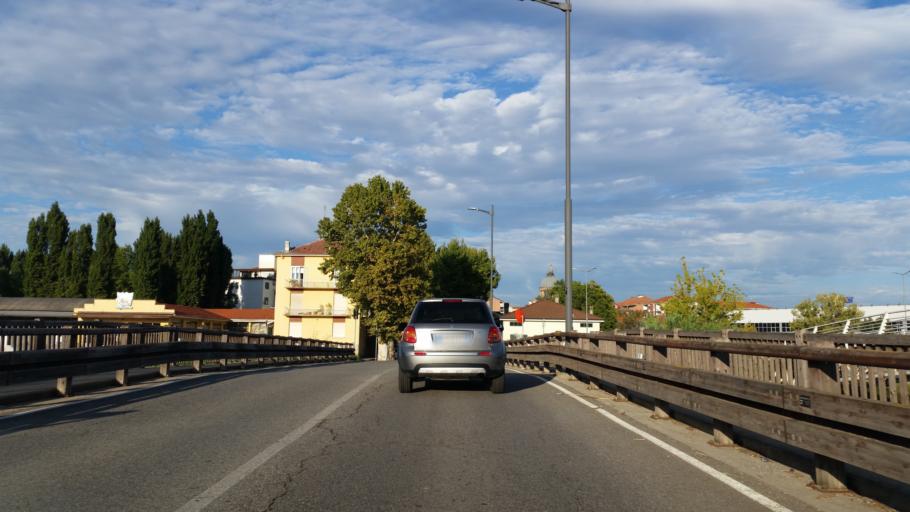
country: IT
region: Piedmont
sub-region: Provincia di Asti
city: Asti
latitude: 44.8962
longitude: 8.1911
